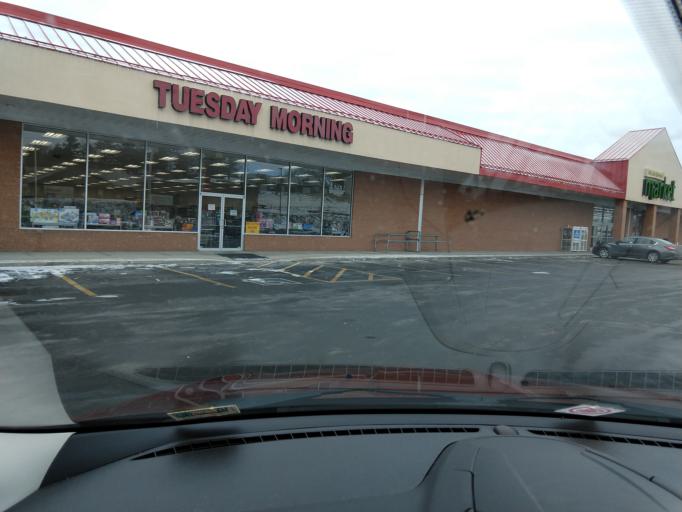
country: US
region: West Virginia
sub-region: Mercer County
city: Bluefield
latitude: 37.2437
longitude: -81.2396
